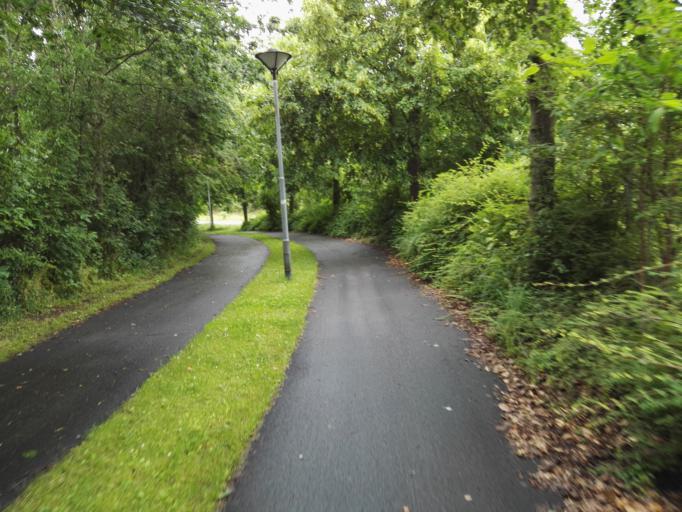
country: DK
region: Capital Region
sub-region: Egedal Kommune
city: Olstykke
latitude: 55.7785
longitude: 12.1609
